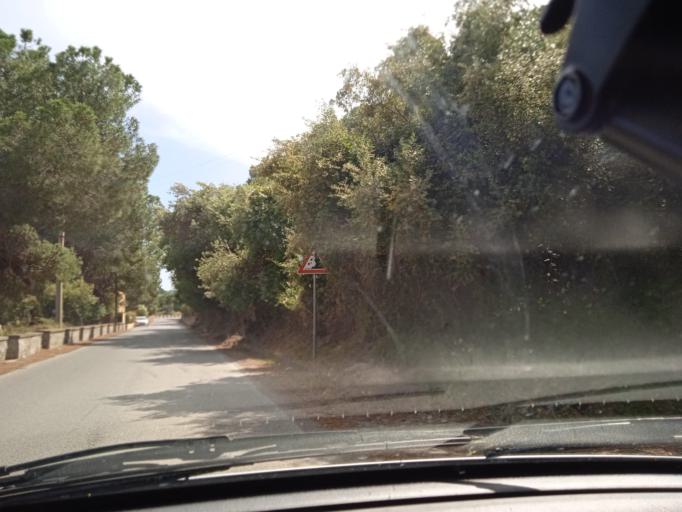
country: IT
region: Sicily
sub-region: Messina
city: Milazzo
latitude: 38.2429
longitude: 15.2515
